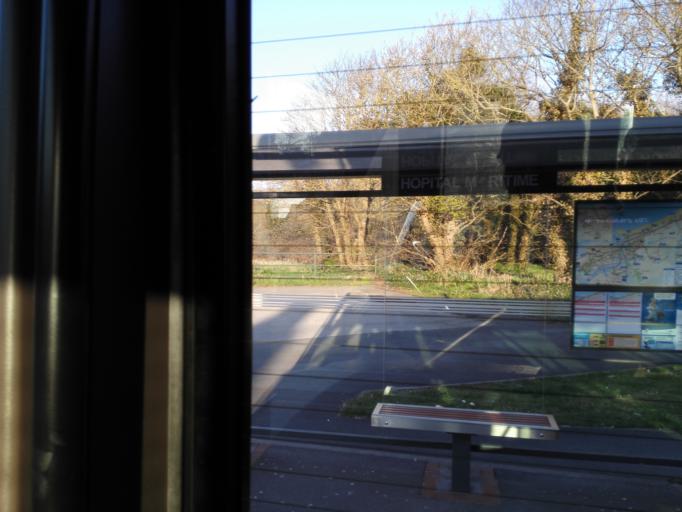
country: FR
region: Nord-Pas-de-Calais
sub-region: Departement du Nord
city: Zuydcoote
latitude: 51.0663
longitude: 2.4804
